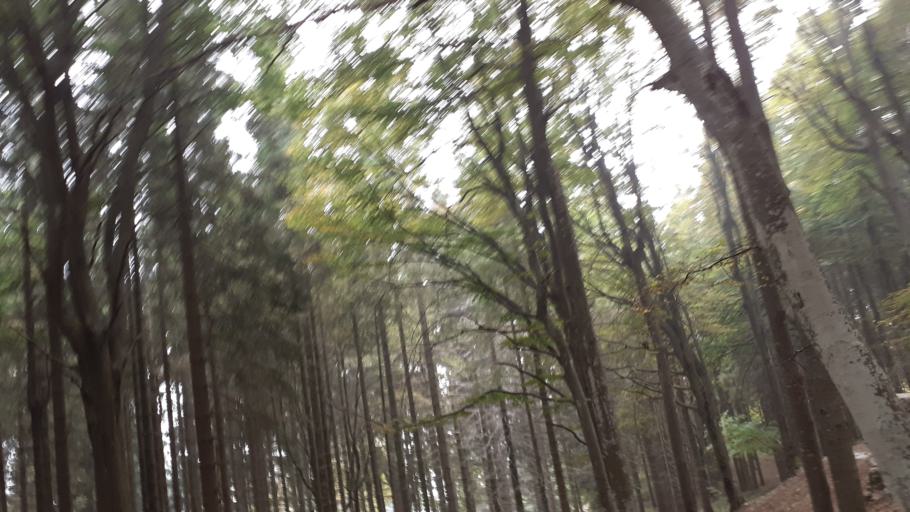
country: IT
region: Lombardy
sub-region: Provincia di Lecco
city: Ballabio
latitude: 45.9114
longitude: 9.3955
